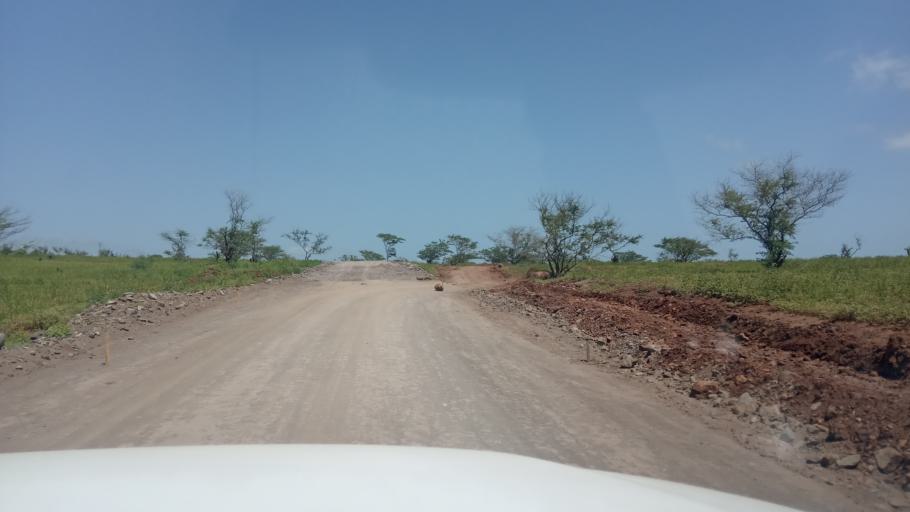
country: CV
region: Ribeira Grande de Santiago
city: Cidade Velha
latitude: 14.9219
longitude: -23.6126
